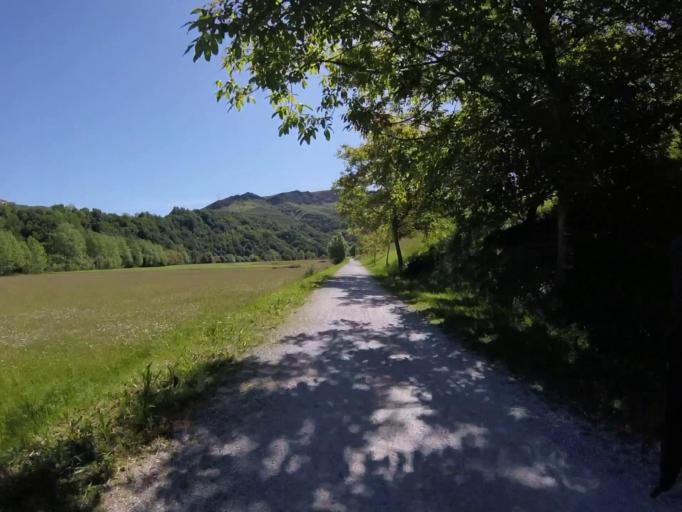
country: ES
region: Basque Country
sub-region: Provincia de Guipuzcoa
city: Irun
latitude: 43.3304
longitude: -1.7457
